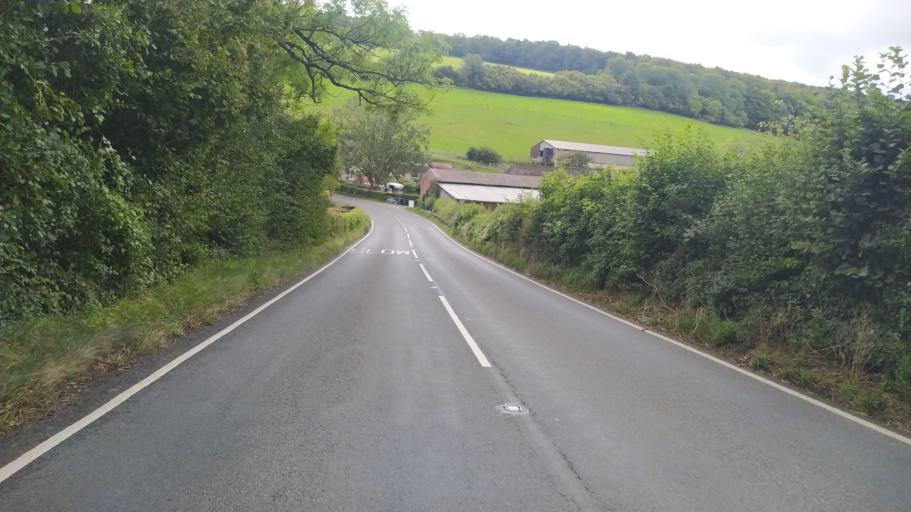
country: GB
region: England
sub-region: Dorset
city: Blandford Forum
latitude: 50.8848
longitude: -2.2167
